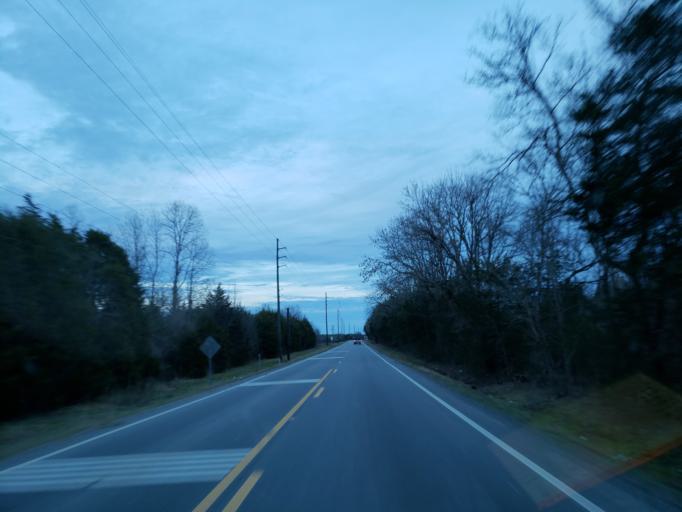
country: US
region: Alabama
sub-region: Sumter County
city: Livingston
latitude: 32.8037
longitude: -88.3107
